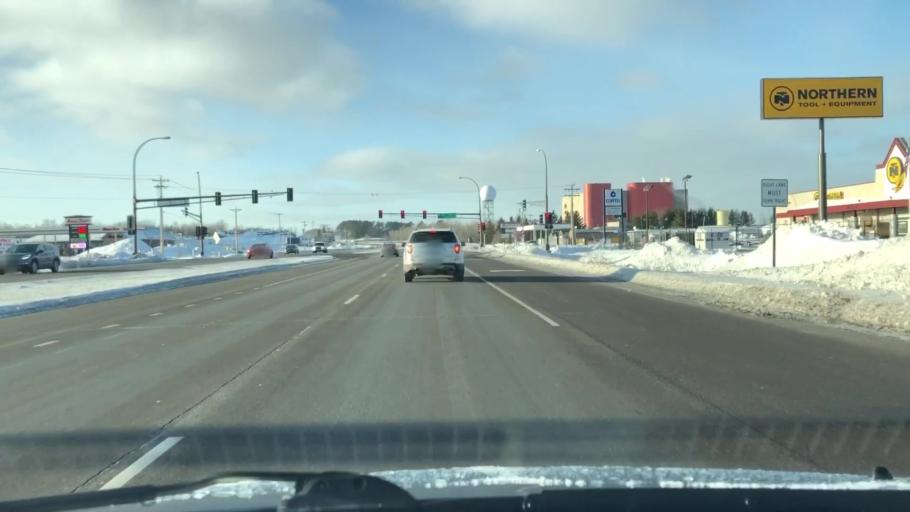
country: US
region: Minnesota
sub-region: Saint Louis County
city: Hermantown
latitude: 46.8330
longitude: -92.2043
